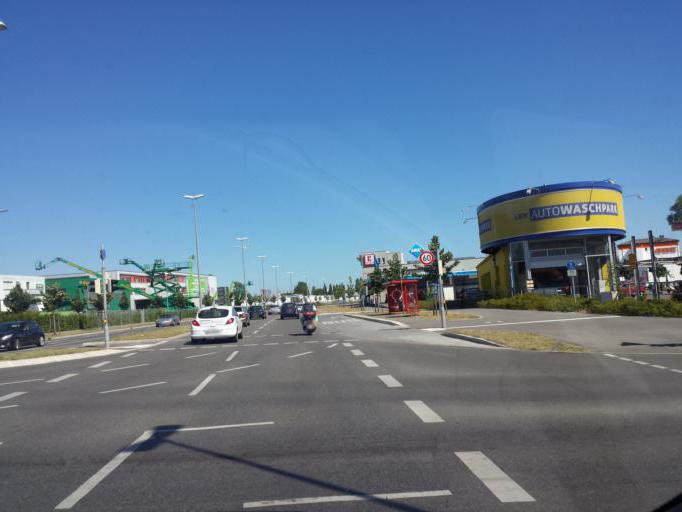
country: CH
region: Thurgau
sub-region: Kreuzlingen District
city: Gottlieben
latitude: 47.6782
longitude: 9.1454
